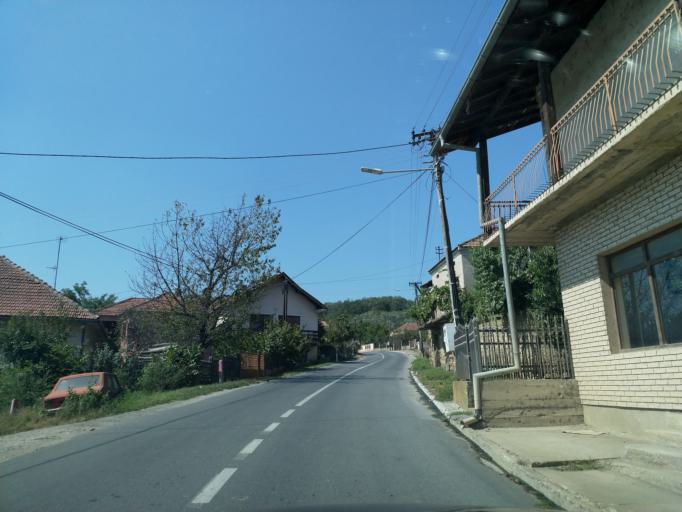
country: RS
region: Central Serbia
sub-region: Rasinski Okrug
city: Krusevac
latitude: 43.6243
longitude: 21.3591
